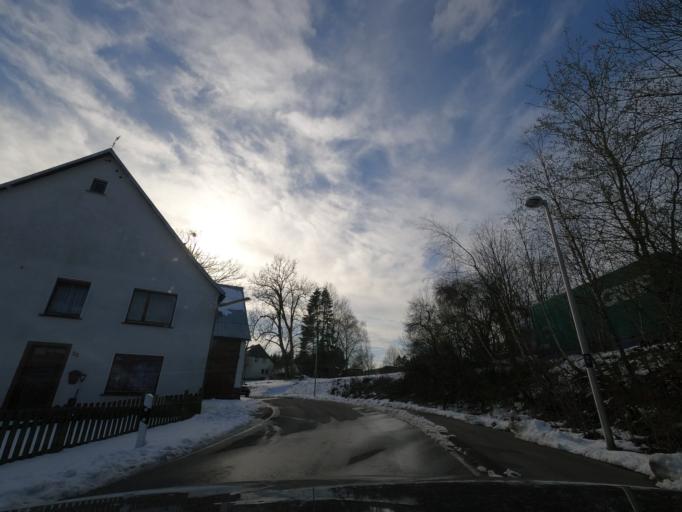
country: DE
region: North Rhine-Westphalia
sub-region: Regierungsbezirk Arnsberg
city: Herscheid
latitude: 51.1251
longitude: 7.7693
